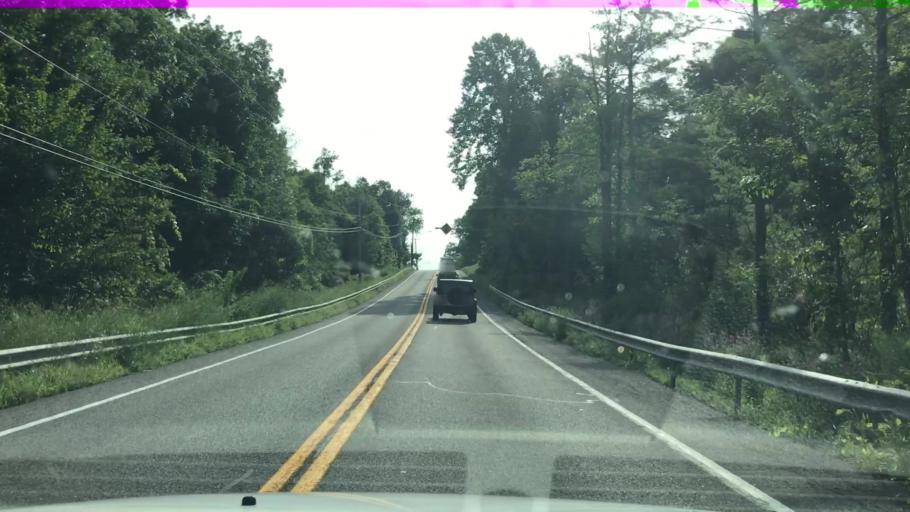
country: US
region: New York
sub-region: Erie County
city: Town Line
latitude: 42.8563
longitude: -78.5814
